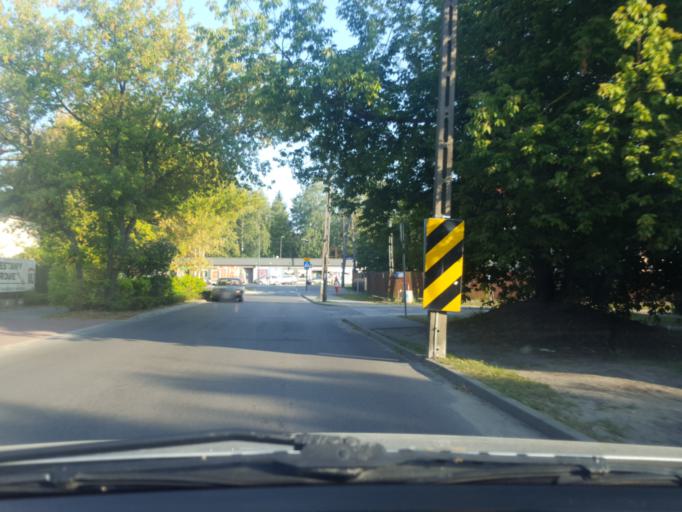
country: PL
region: Masovian Voivodeship
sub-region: Warszawa
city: Rembertow
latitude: 52.2652
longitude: 21.1688
